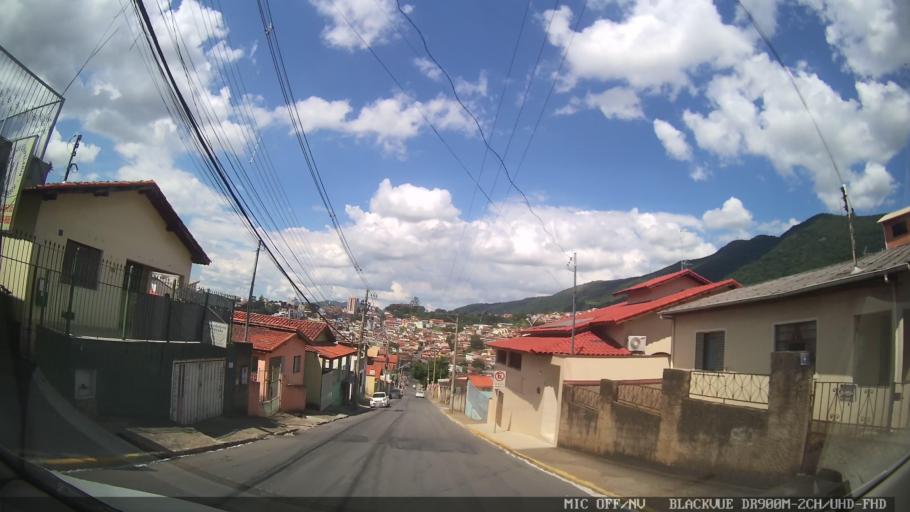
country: BR
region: Minas Gerais
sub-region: Extrema
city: Extrema
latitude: -22.8607
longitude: -46.3266
